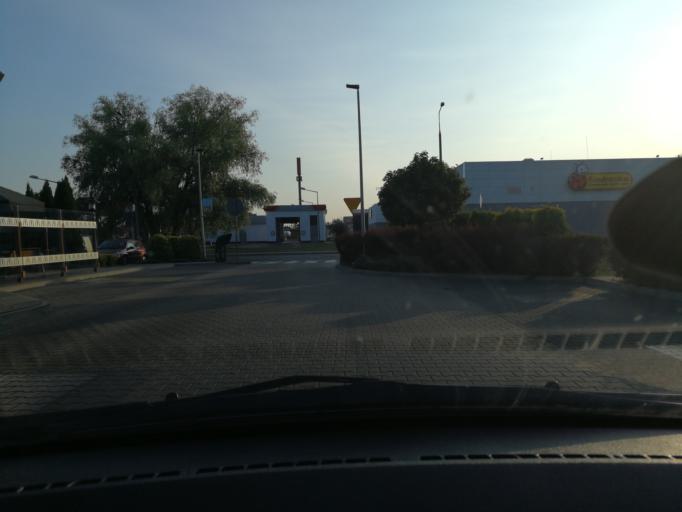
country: PL
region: Lodz Voivodeship
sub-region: Skierniewice
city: Skierniewice
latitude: 51.9724
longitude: 20.1494
